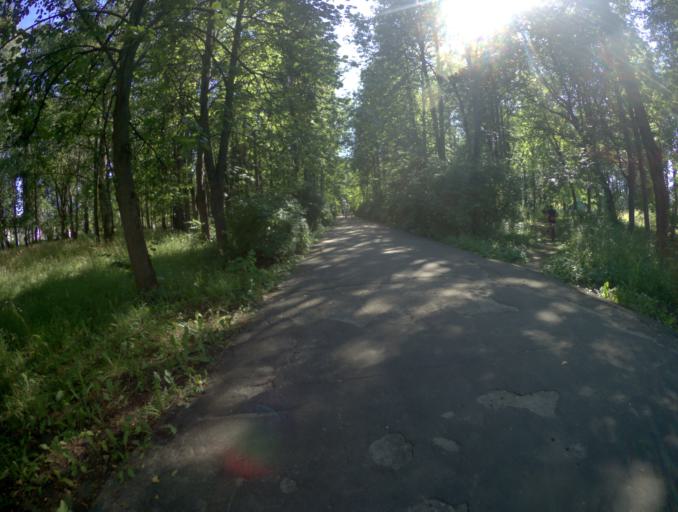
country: RU
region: Nizjnij Novgorod
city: Pavlovo
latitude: 55.9759
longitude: 43.0870
